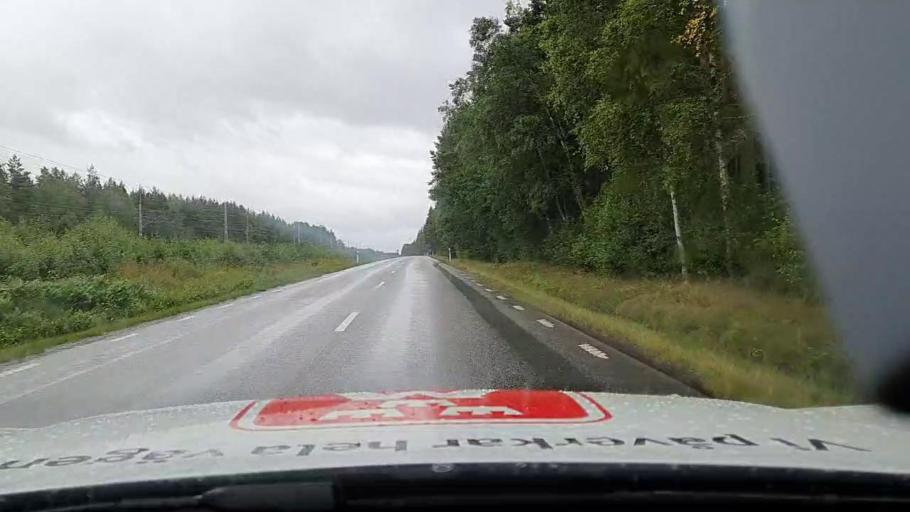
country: SE
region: Vaestra Goetaland
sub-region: Toreboda Kommun
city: Toereboda
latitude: 58.6682
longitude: 14.0939
